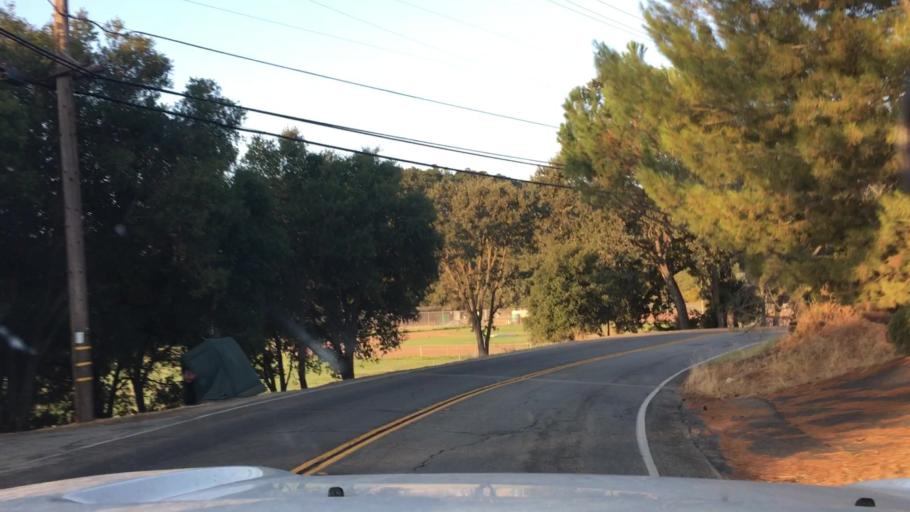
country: US
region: California
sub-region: San Luis Obispo County
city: Atascadero
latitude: 35.4844
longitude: -120.6747
